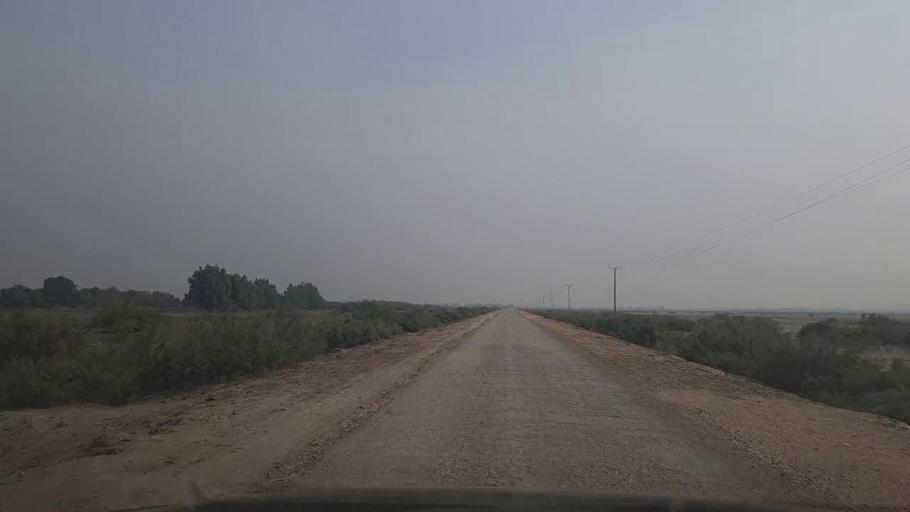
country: PK
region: Sindh
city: Mirpur Sakro
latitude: 24.4608
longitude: 67.6940
